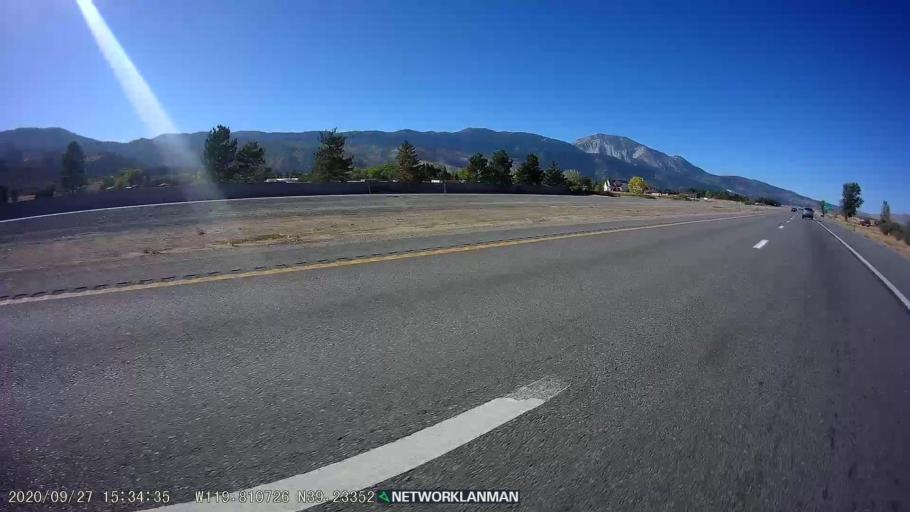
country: US
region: Nevada
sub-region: Carson City
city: Carson City
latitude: 39.2340
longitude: -119.8107
